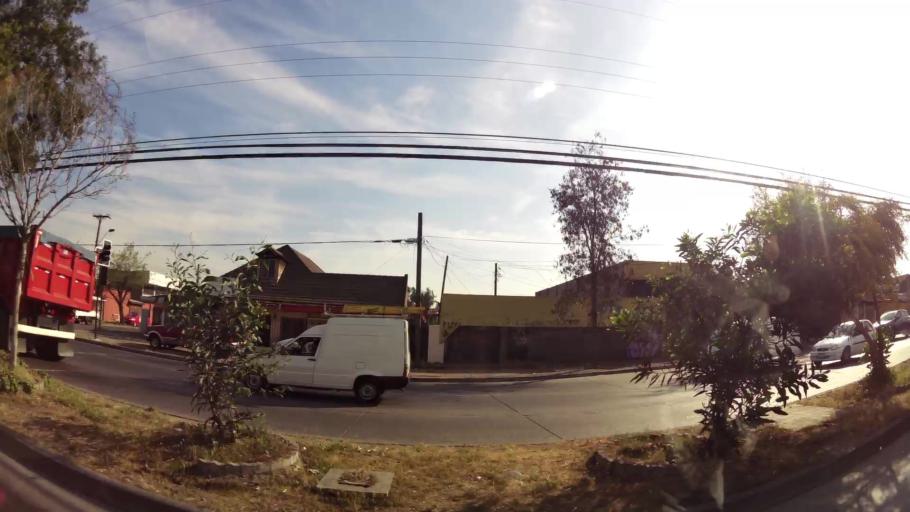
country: CL
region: Santiago Metropolitan
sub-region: Provincia de Santiago
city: Santiago
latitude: -33.5059
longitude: -70.6449
